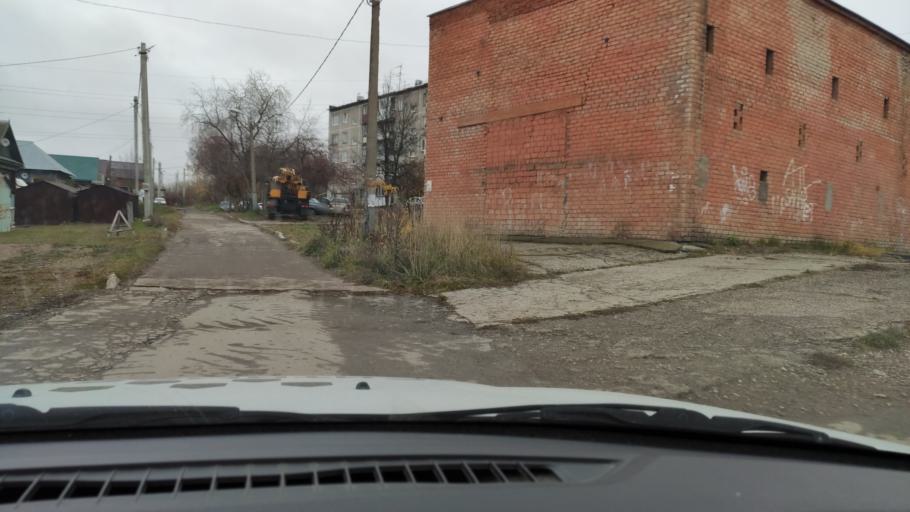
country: RU
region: Perm
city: Kondratovo
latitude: 57.9607
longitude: 56.1480
